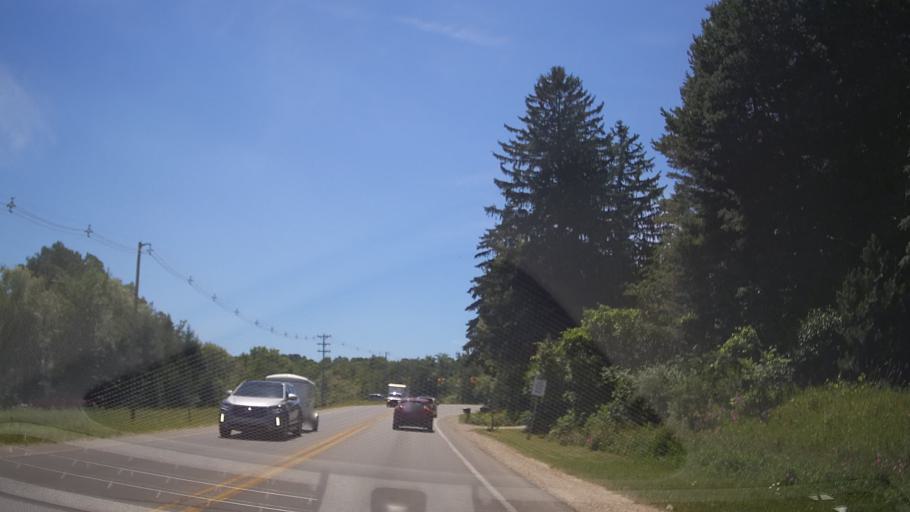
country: US
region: Michigan
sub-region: Grand Traverse County
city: Traverse City
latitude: 44.7297
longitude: -85.6628
